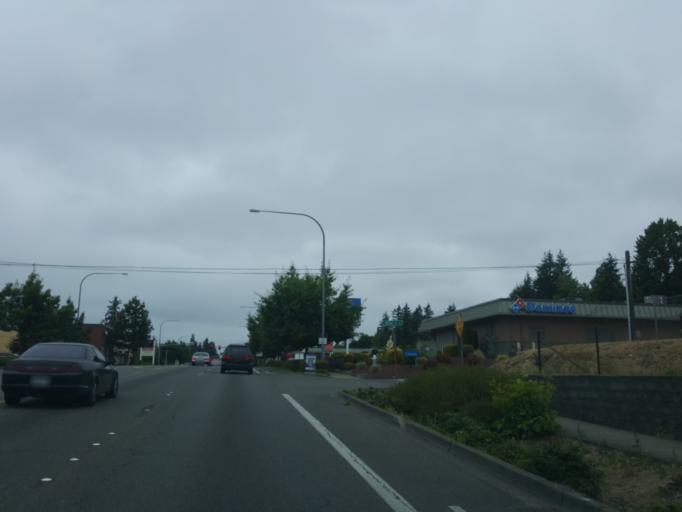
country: US
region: Washington
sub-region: Pierce County
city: Parkland
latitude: 47.1441
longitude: -122.4344
